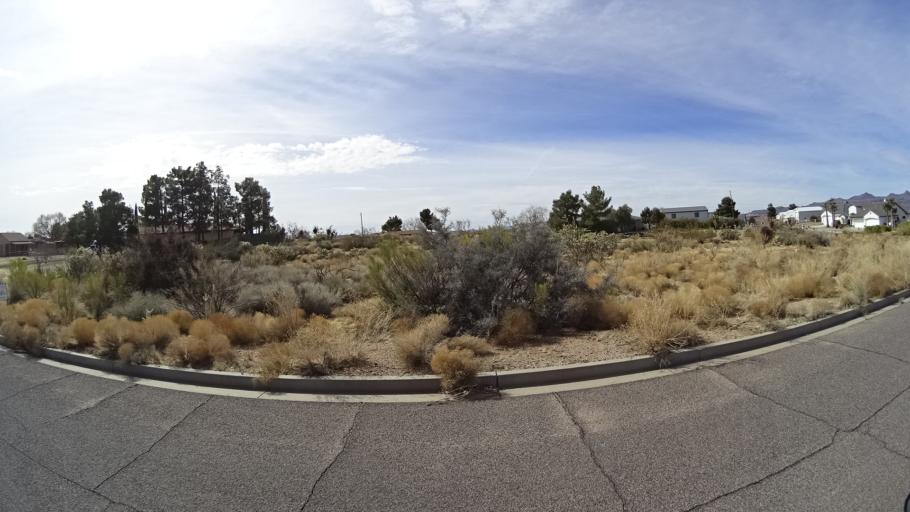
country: US
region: Arizona
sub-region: Mohave County
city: Kingman
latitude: 35.1857
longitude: -113.9901
